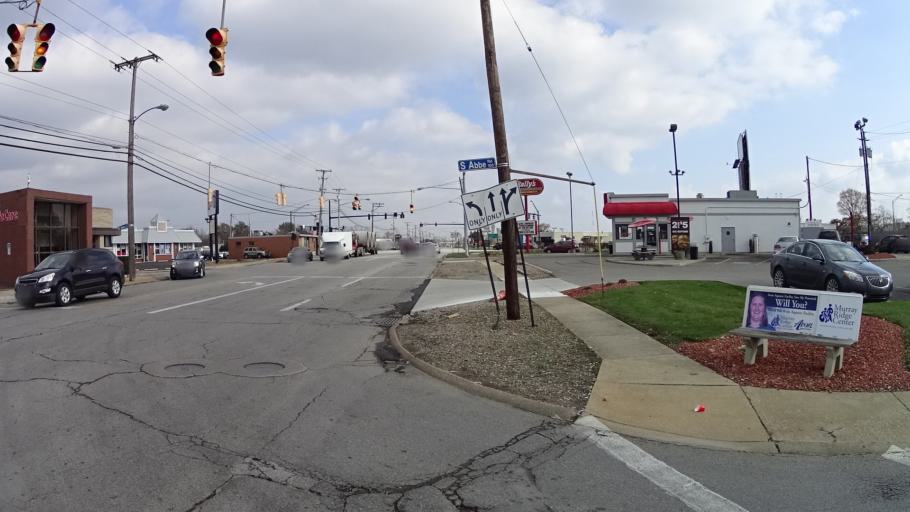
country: US
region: Ohio
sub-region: Lorain County
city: Elyria
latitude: 41.3772
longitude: -82.0776
